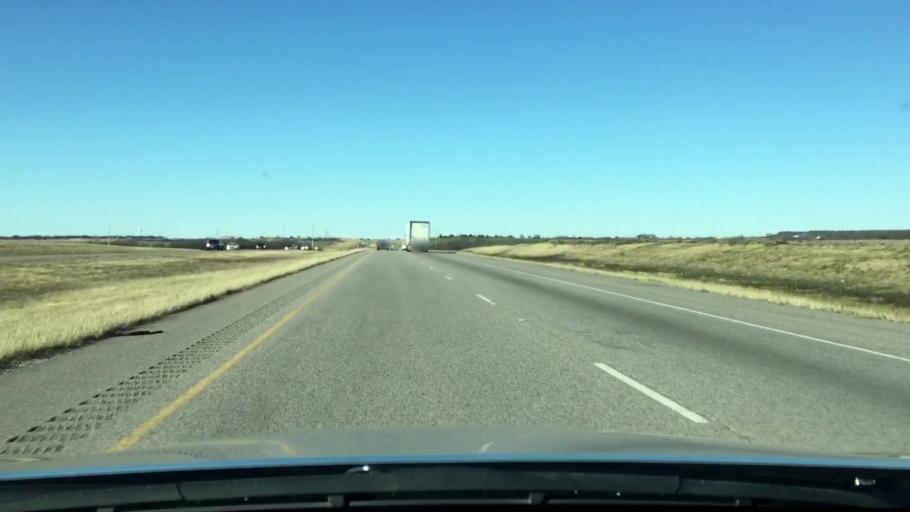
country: US
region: Texas
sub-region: Hill County
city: Itasca
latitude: 32.1283
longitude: -97.1185
